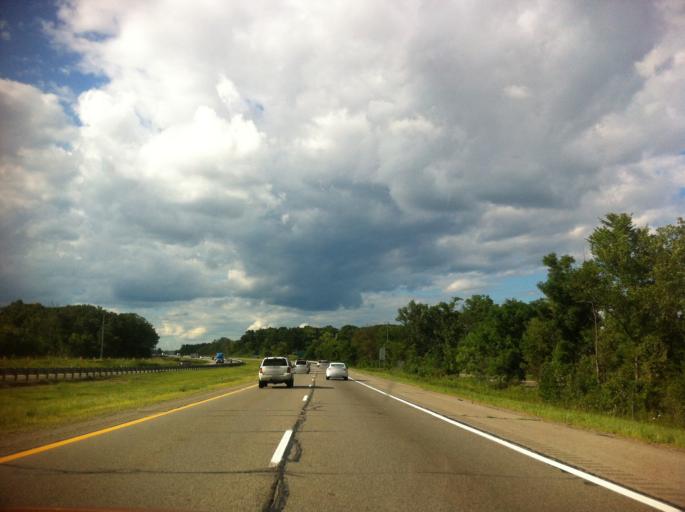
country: US
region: Michigan
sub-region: Livingston County
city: Whitmore Lake
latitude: 42.4513
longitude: -83.7521
